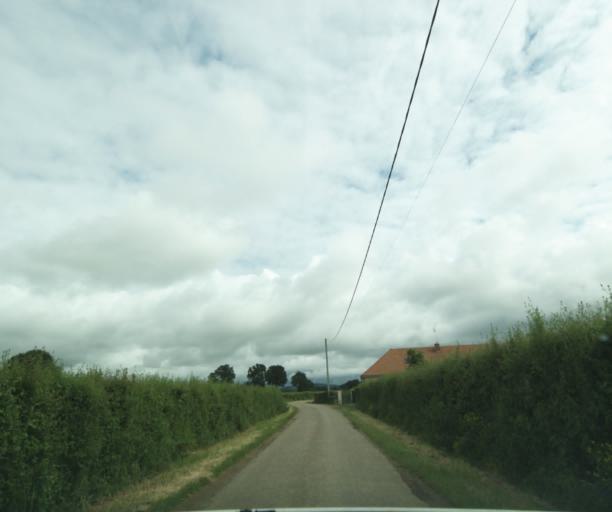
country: FR
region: Bourgogne
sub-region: Departement de Saone-et-Loire
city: Charolles
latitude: 46.4237
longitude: 4.3144
